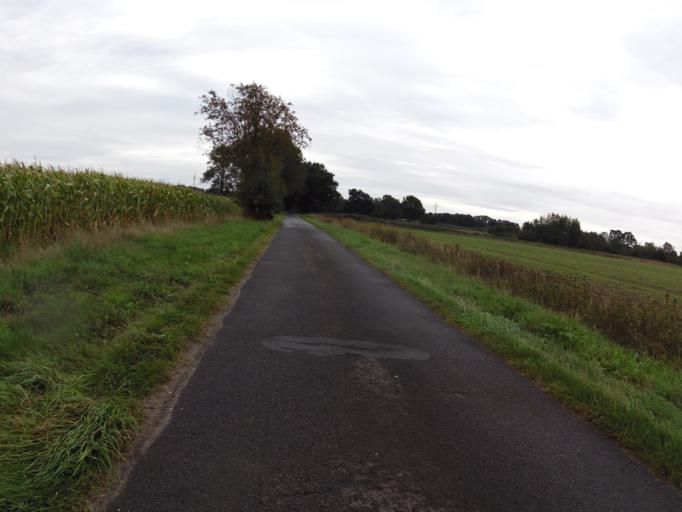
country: DE
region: Lower Saxony
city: Hamersen
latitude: 53.2661
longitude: 9.4737
